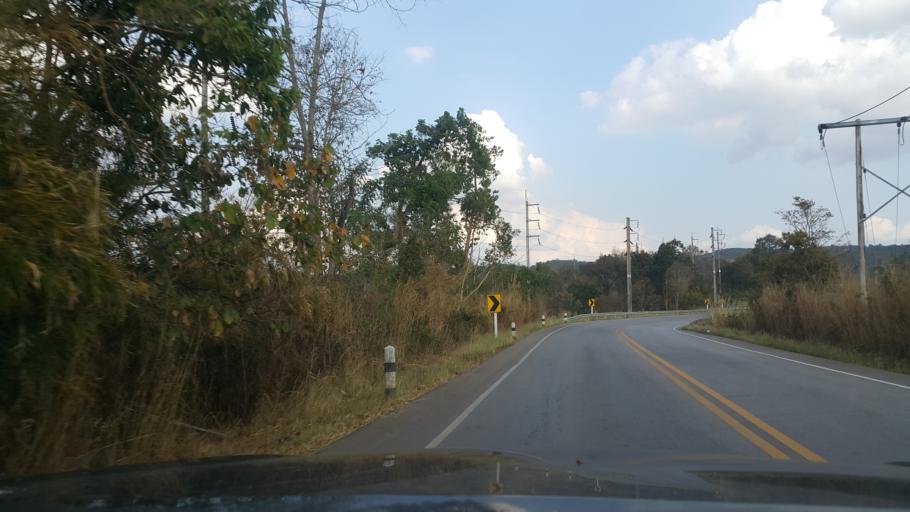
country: TH
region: Loei
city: Dan Sai
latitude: 17.2407
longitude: 101.1085
